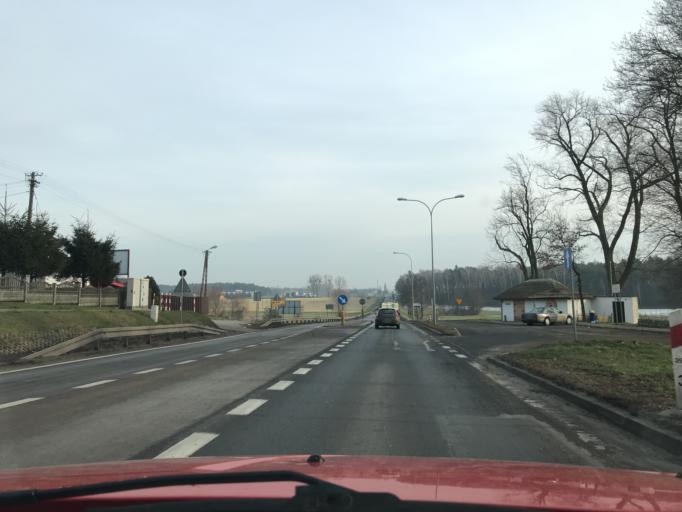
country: PL
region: Greater Poland Voivodeship
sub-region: Powiat jarocinski
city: Witaszyce
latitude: 51.9374
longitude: 17.6059
